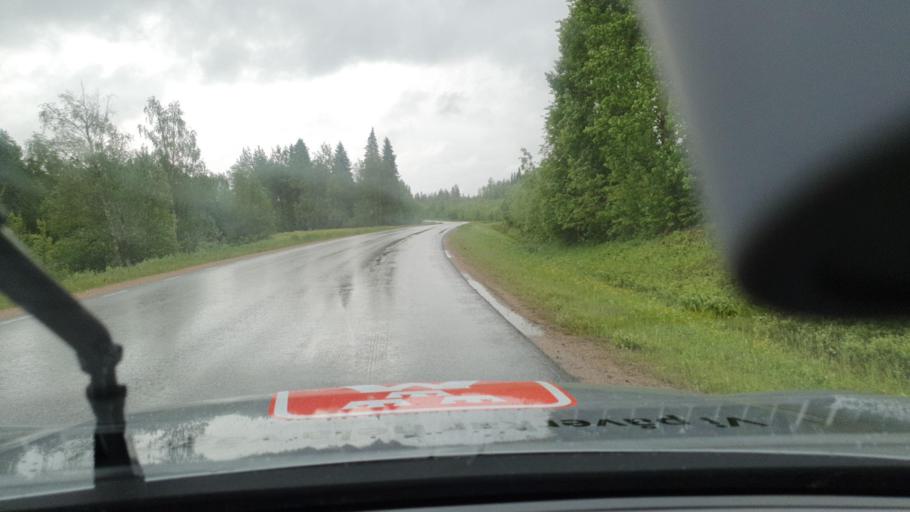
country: FI
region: Lapland
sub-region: Torniolaakso
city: Ylitornio
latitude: 66.2598
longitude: 23.6542
